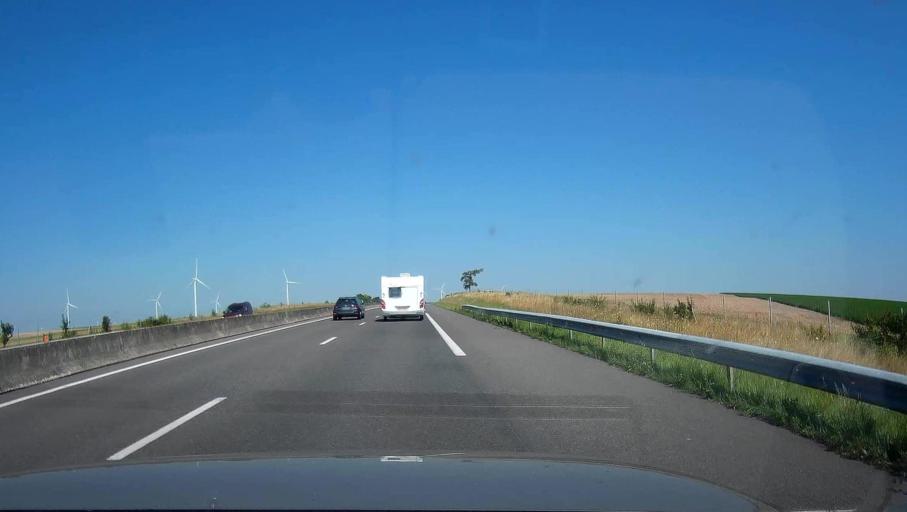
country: FR
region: Champagne-Ardenne
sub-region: Departement de l'Aube
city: Mailly-le-Camp
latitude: 48.6055
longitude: 4.1800
